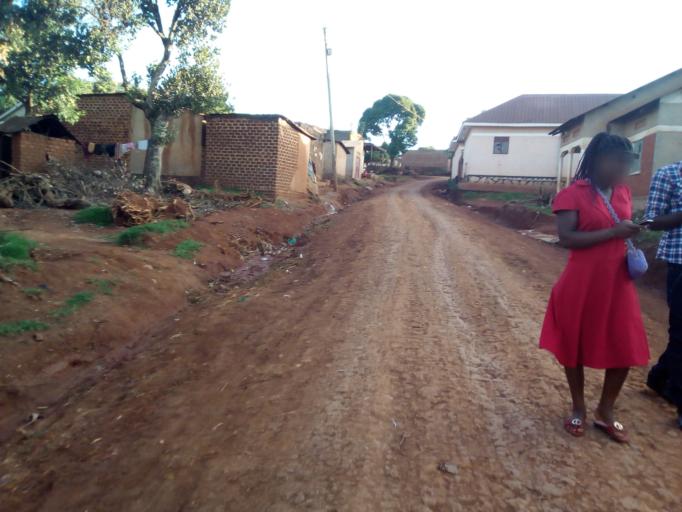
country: UG
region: Central Region
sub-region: Kampala District
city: Kampala
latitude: 0.2503
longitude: 32.5764
